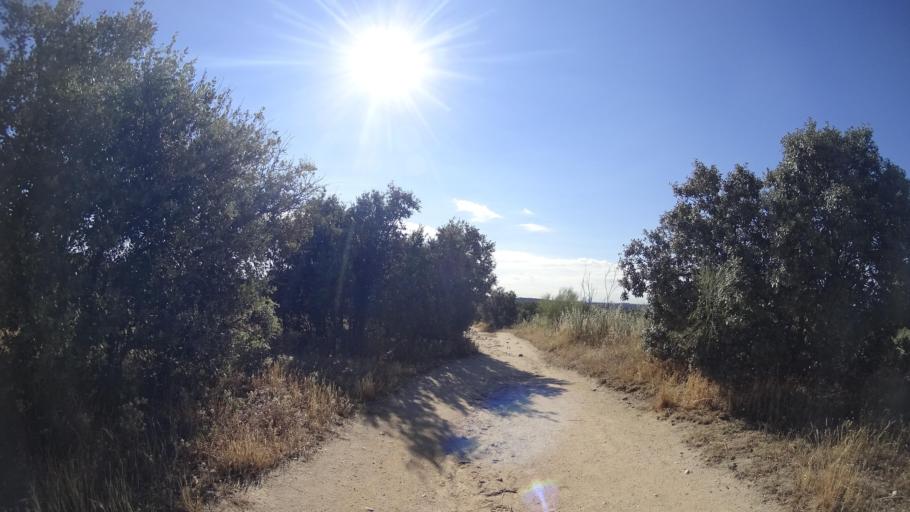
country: ES
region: Madrid
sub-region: Provincia de Madrid
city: Las Matas
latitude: 40.5517
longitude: -3.8831
